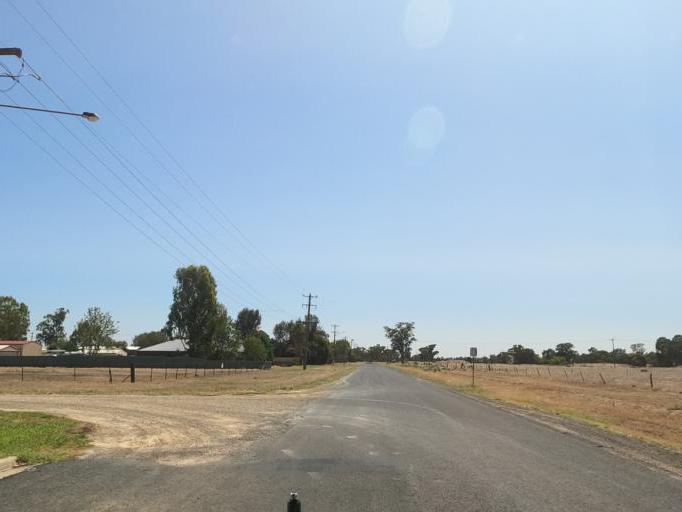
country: AU
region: New South Wales
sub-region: Corowa Shire
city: Mulwala
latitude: -35.9823
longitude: 146.0018
